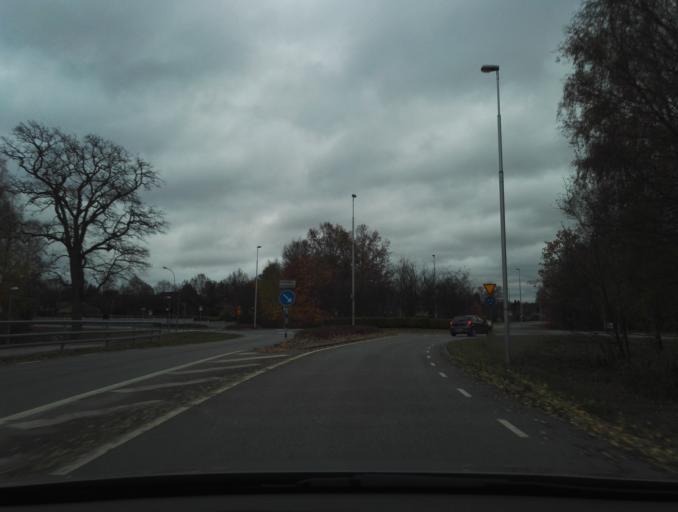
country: SE
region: Kronoberg
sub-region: Vaxjo Kommun
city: Vaexjoe
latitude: 56.8602
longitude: 14.8101
